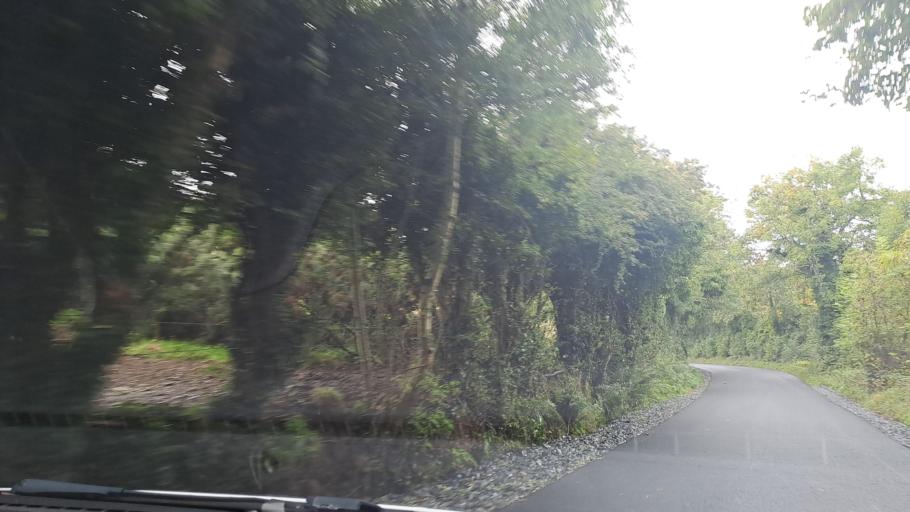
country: IE
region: Ulster
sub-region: An Cabhan
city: Kingscourt
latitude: 53.9810
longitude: -6.7960
